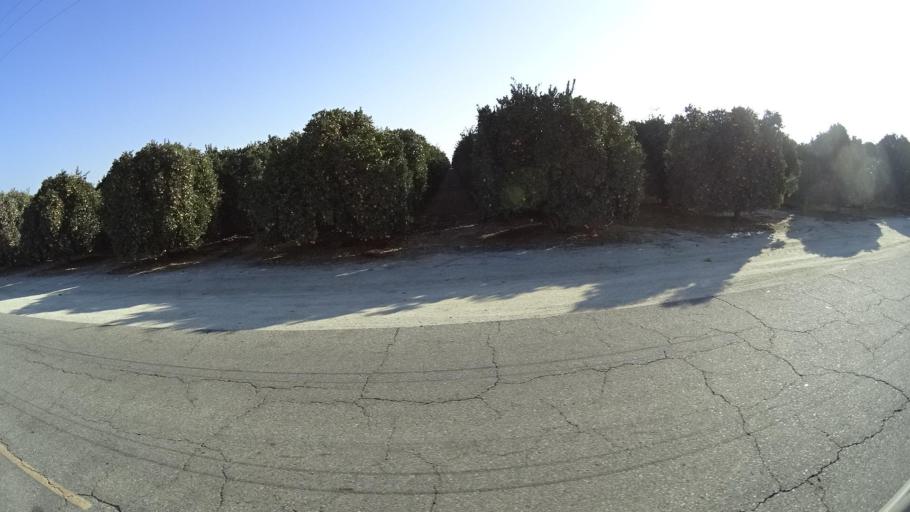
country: US
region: California
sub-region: Tulare County
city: Richgrove
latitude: 35.7846
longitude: -119.1697
